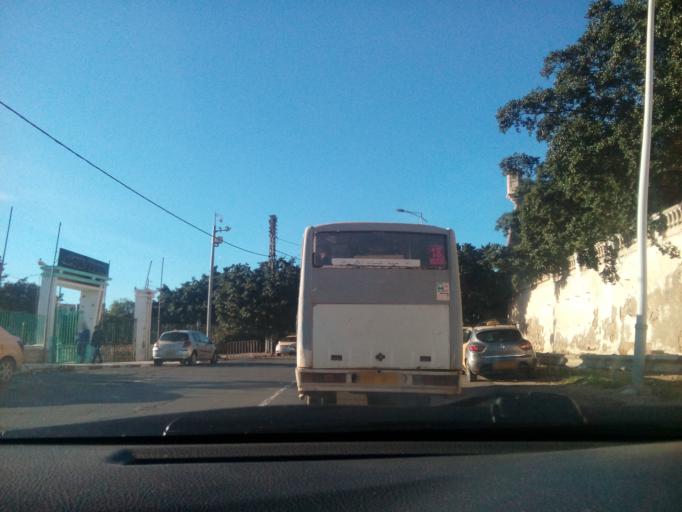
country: DZ
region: Oran
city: Oran
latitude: 35.7076
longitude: -0.6448
